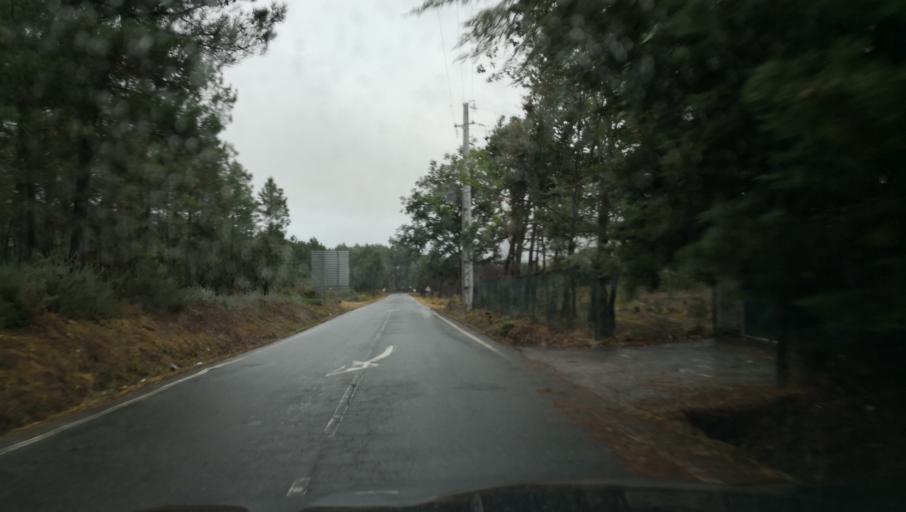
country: PT
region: Vila Real
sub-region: Sabrosa
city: Sabrosa
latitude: 41.3479
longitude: -7.5971
